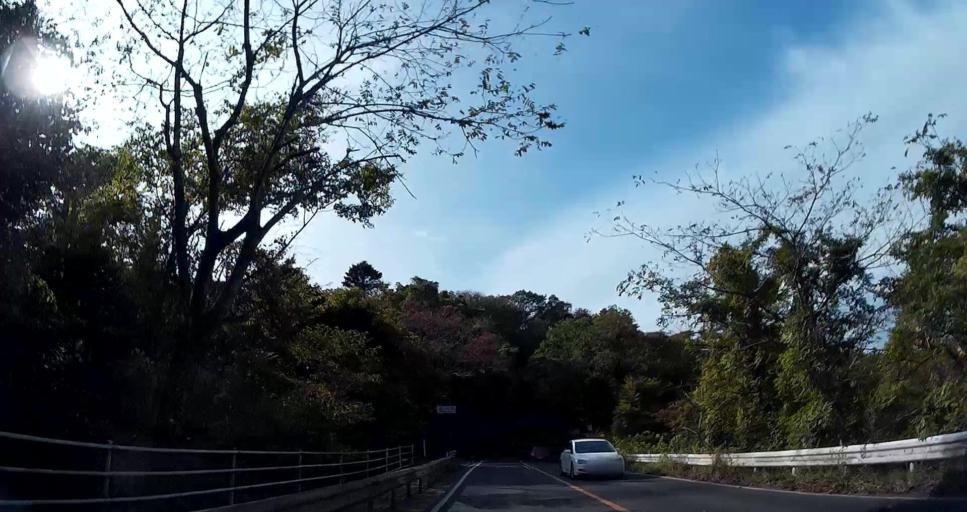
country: JP
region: Miyagi
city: Sendai
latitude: 38.2493
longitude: 140.8513
